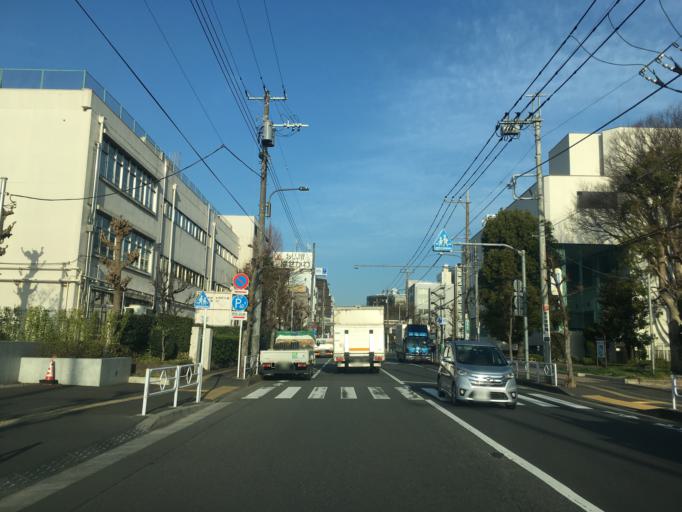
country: JP
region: Tokyo
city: Hino
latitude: 35.6926
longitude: 139.4207
